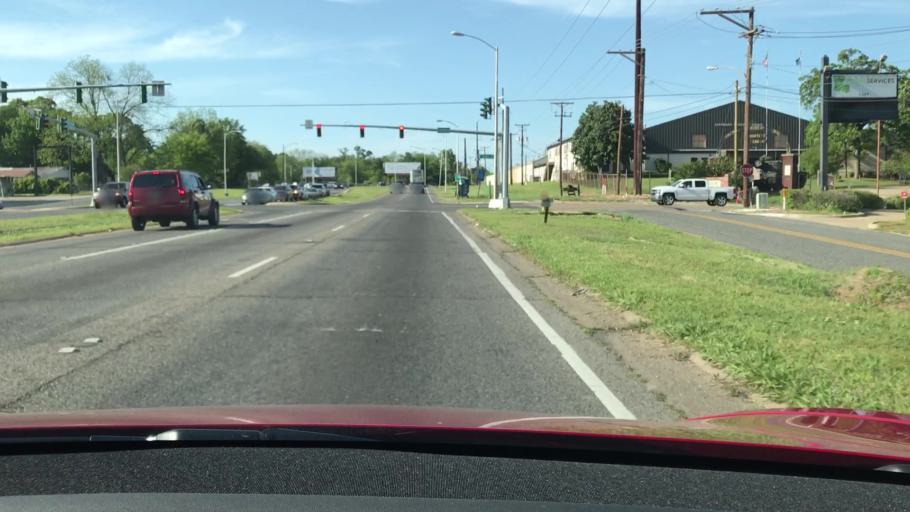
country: US
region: Louisiana
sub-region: Bossier Parish
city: Bossier City
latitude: 32.4995
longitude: -93.7248
